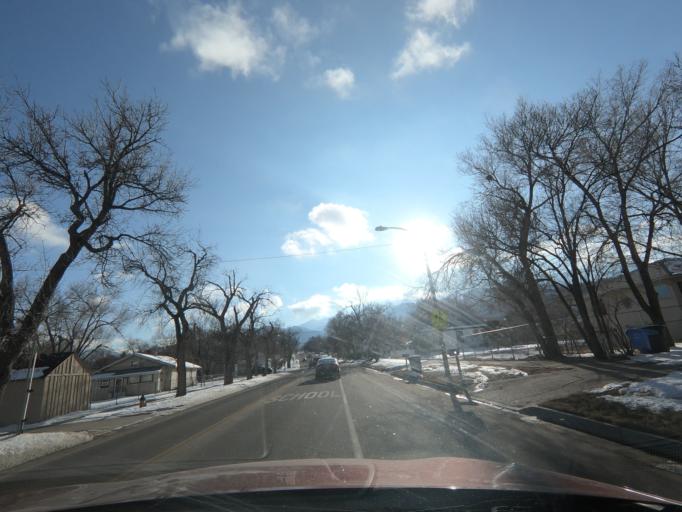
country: US
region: Colorado
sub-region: El Paso County
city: Colorado Springs
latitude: 38.8442
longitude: -104.8681
